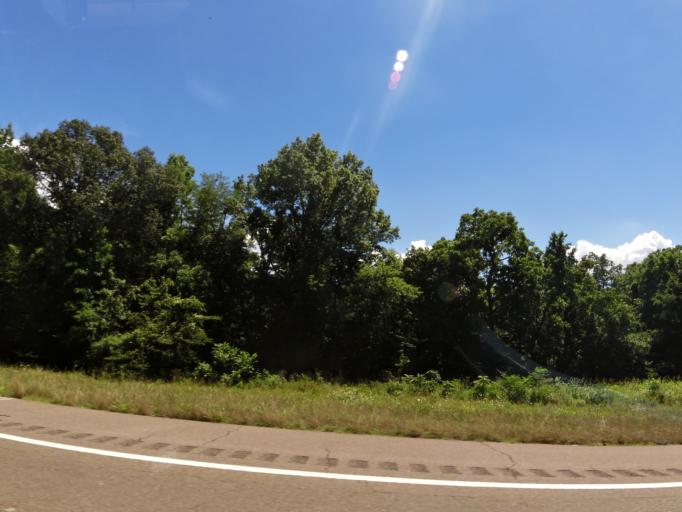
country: US
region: Tennessee
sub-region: Dyer County
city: Dyersburg
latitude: 36.0816
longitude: -89.5337
